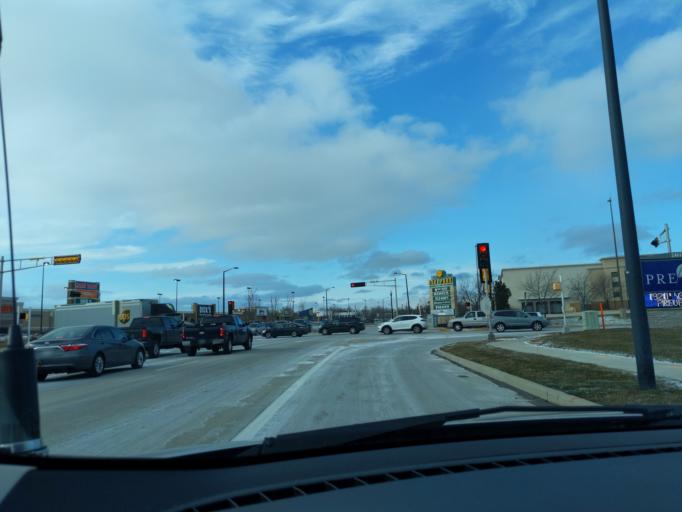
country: US
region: Wisconsin
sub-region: Brown County
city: Ashwaubenon
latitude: 44.4813
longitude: -88.0649
